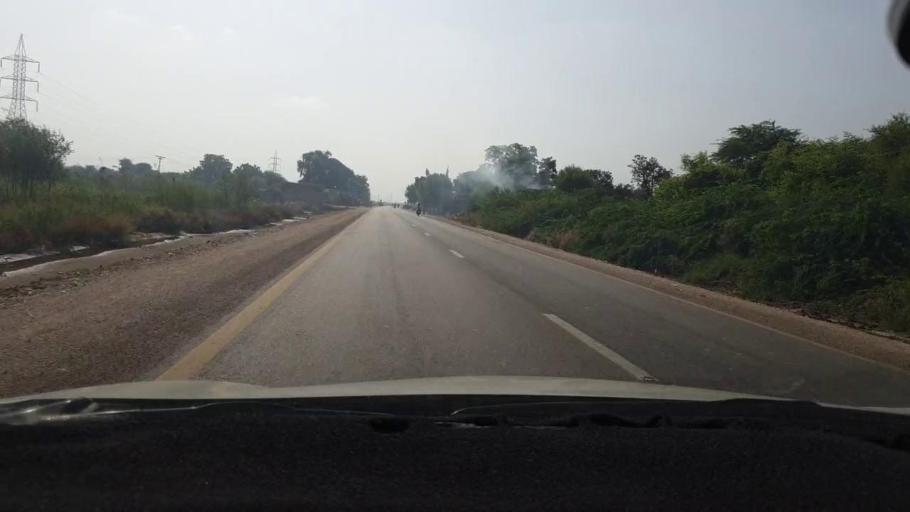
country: PK
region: Sindh
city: Jhol
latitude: 25.9056
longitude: 69.0180
